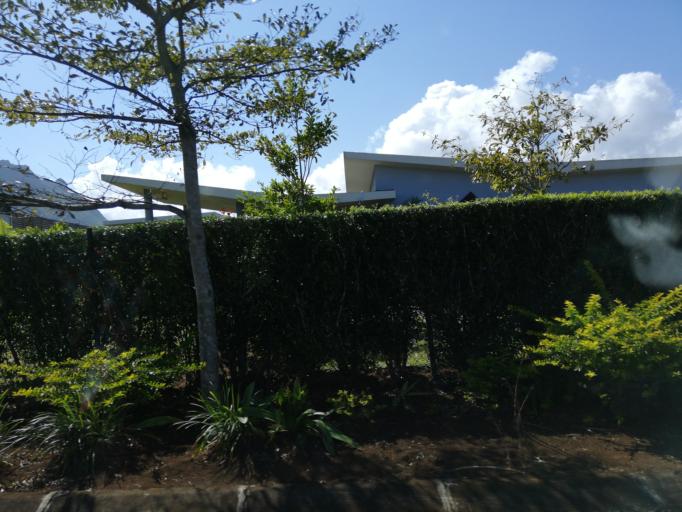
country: MU
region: Moka
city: Moka
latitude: -20.2216
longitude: 57.4985
